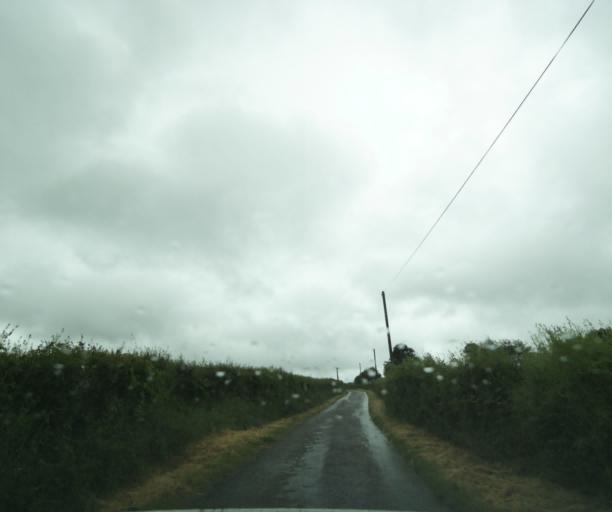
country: FR
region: Bourgogne
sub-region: Departement de Saone-et-Loire
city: Charolles
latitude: 46.4855
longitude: 4.4132
